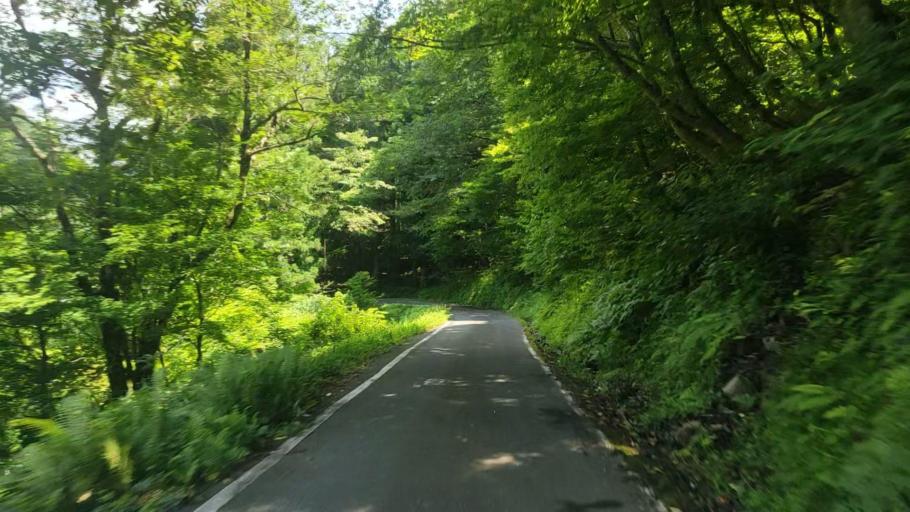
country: JP
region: Fukui
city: Ono
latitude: 35.7662
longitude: 136.5518
